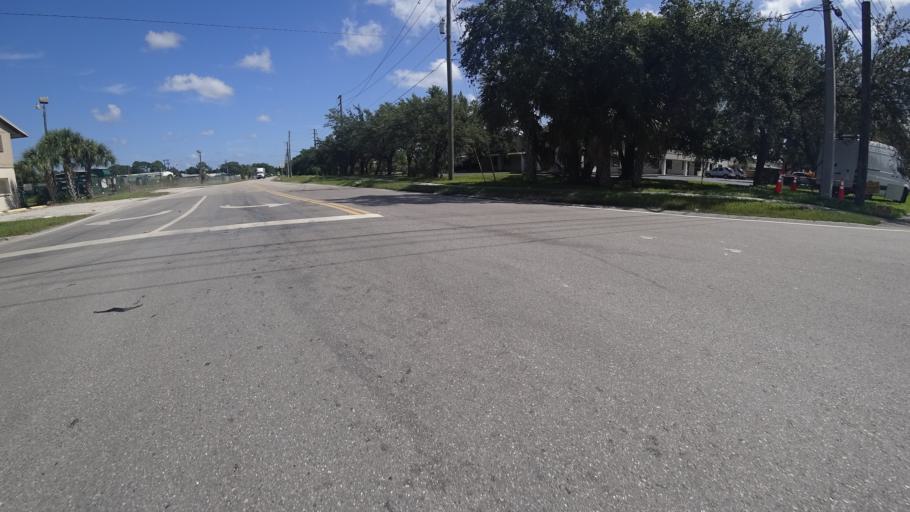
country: US
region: Florida
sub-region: Manatee County
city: Whitfield
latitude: 27.4292
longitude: -82.5384
